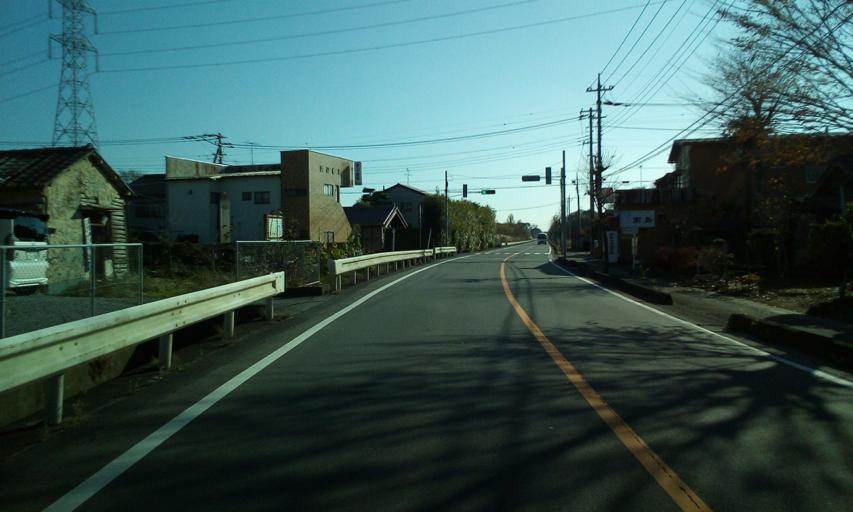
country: JP
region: Saitama
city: Kasukabe
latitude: 36.0036
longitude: 139.7954
